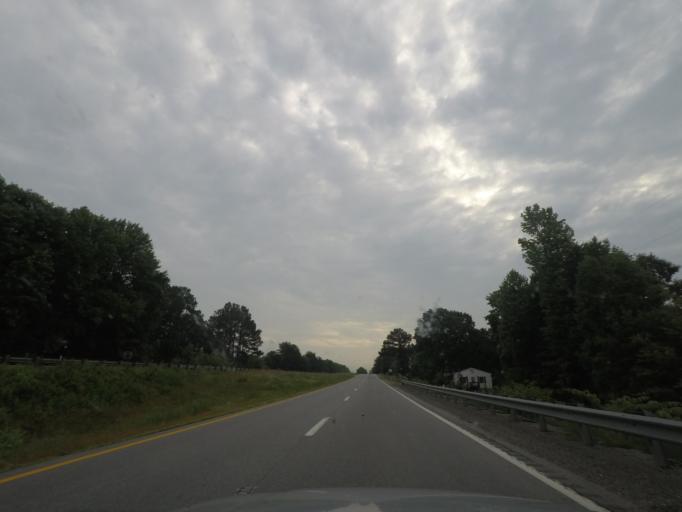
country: US
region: Virginia
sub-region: Mecklenburg County
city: Chase City
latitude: 36.8916
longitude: -78.5478
